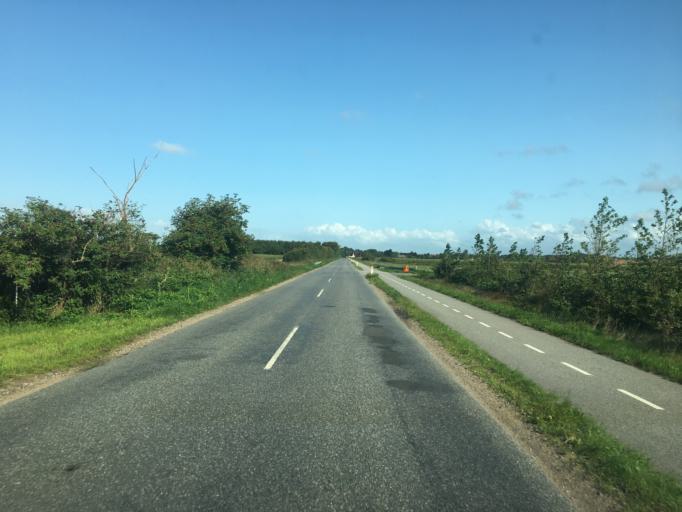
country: DK
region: South Denmark
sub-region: Tonder Kommune
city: Sherrebek
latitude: 55.1433
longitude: 8.7594
